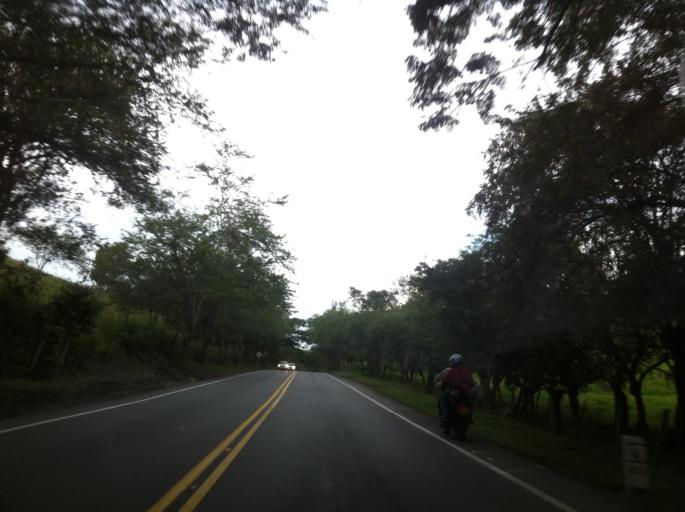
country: CO
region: Valle del Cauca
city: Zarzal
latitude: 4.3506
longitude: -76.0402
